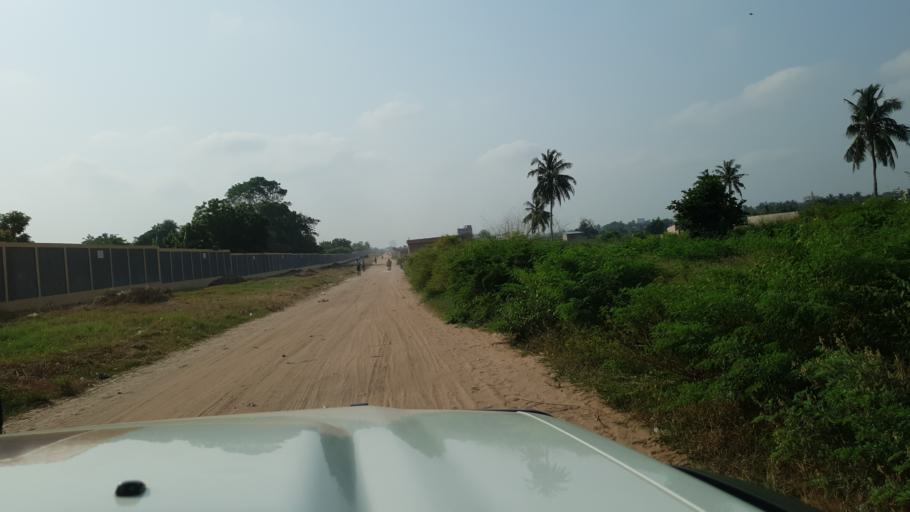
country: TG
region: Maritime
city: Lome
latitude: 6.1762
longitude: 1.2093
